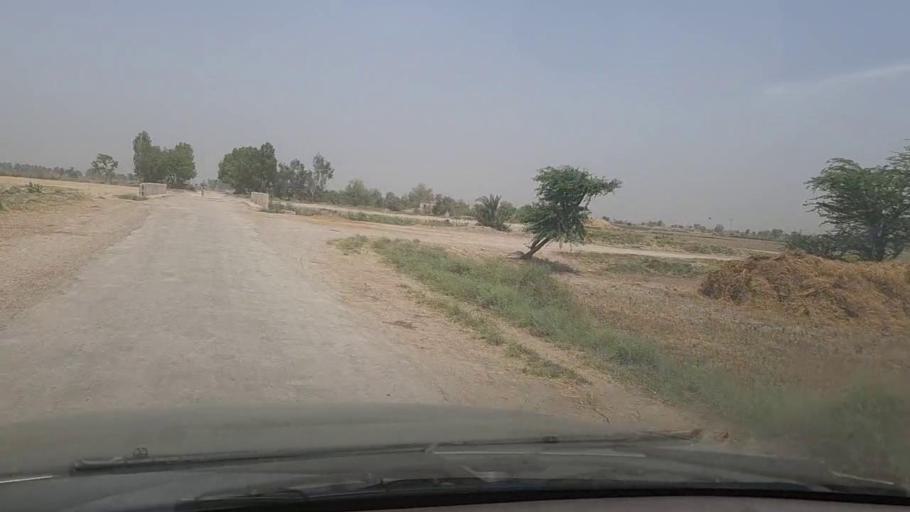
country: PK
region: Sindh
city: Madeji
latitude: 27.8295
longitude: 68.3905
